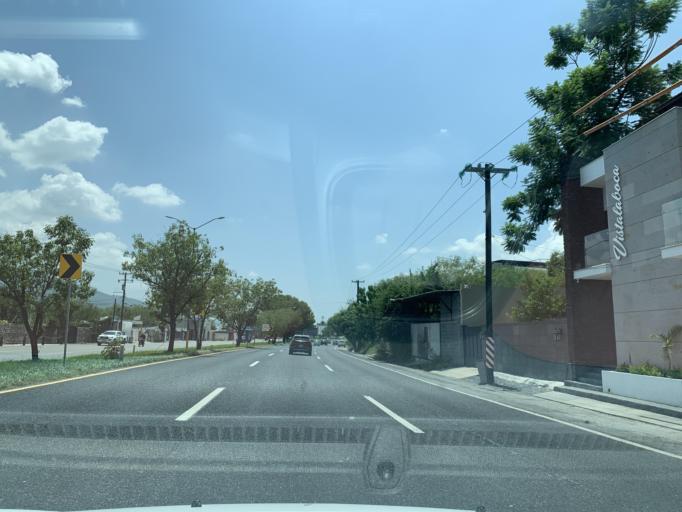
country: MX
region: Nuevo Leon
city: Santiago
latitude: 25.4189
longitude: -100.1434
